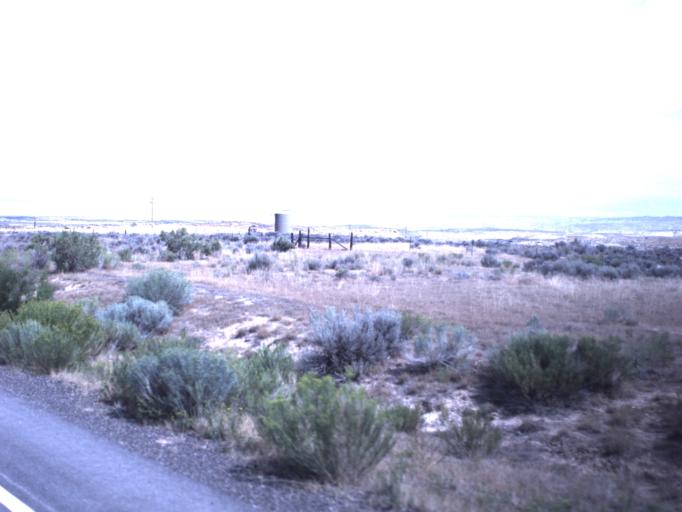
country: US
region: Utah
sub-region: Uintah County
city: Naples
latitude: 40.2044
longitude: -109.3571
